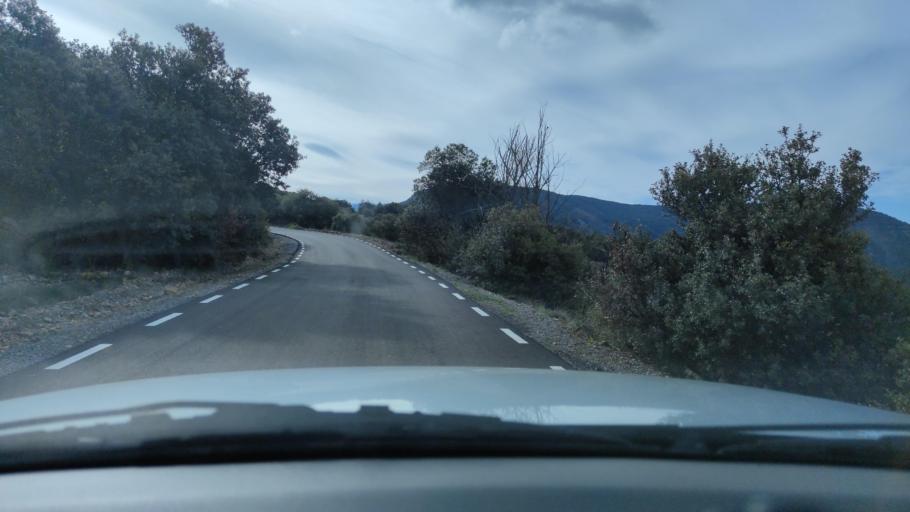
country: ES
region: Catalonia
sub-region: Provincia de Lleida
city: Coll de Nargo
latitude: 42.2379
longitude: 1.4045
